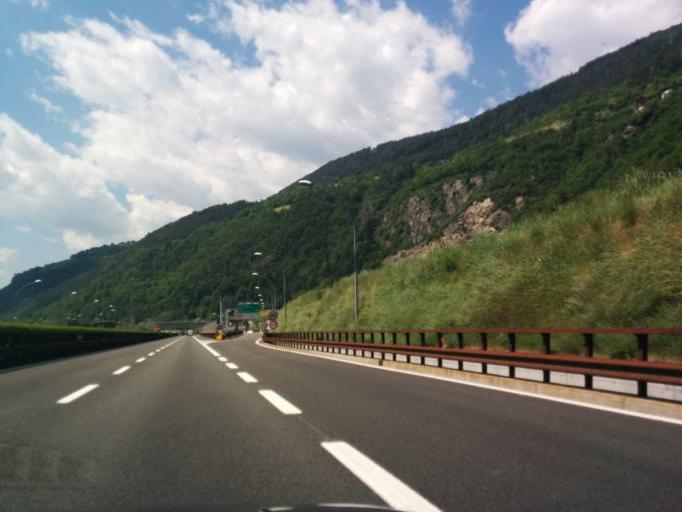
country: IT
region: Trentino-Alto Adige
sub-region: Bolzano
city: Bressanone
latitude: 46.6866
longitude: 11.6308
